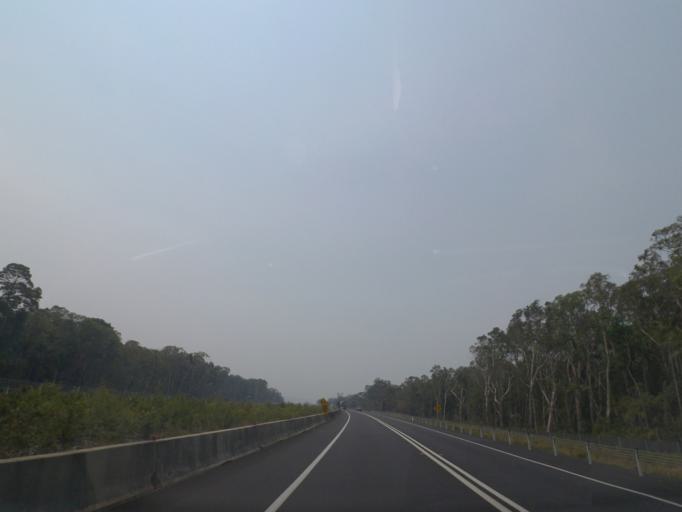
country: AU
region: New South Wales
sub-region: Ballina
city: Ballina
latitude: -28.9137
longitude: 153.4784
